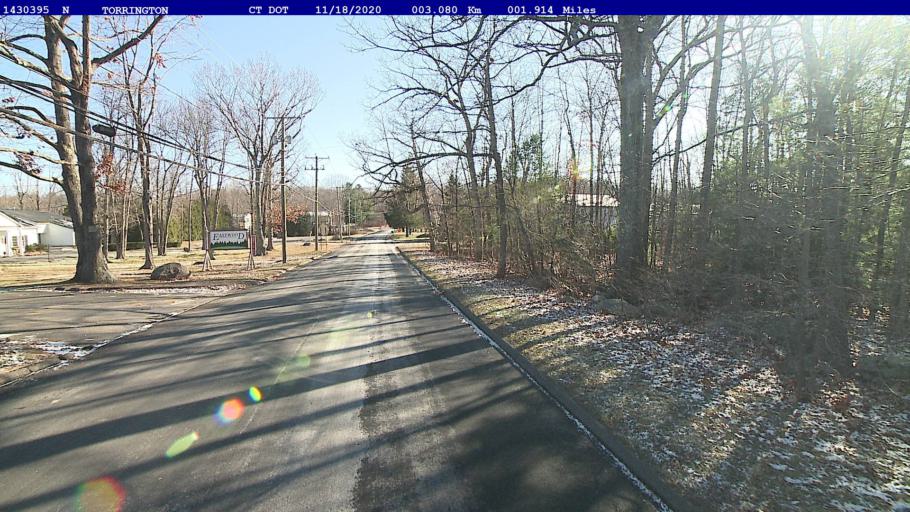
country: US
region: Connecticut
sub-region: Litchfield County
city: Torrington
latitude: 41.8327
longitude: -73.0909
